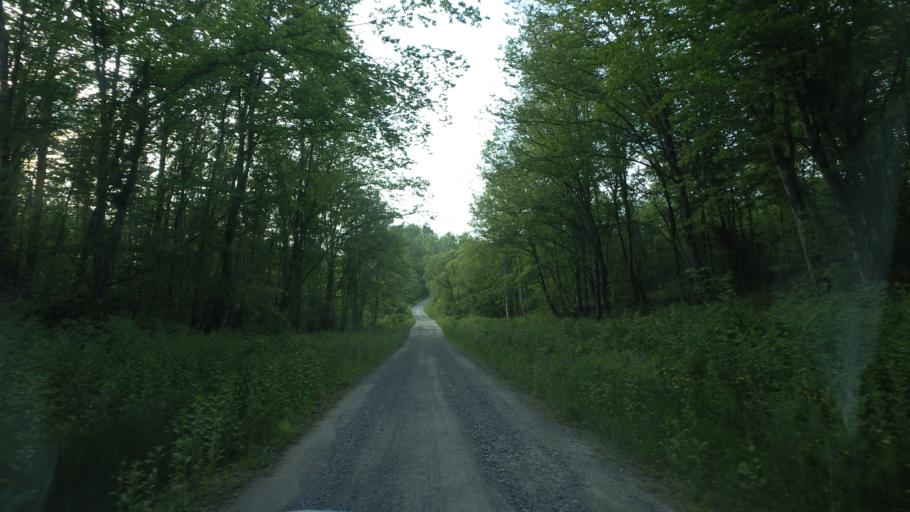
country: HR
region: Sisacko-Moslavacka
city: Gvozd
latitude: 45.3066
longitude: 15.9799
